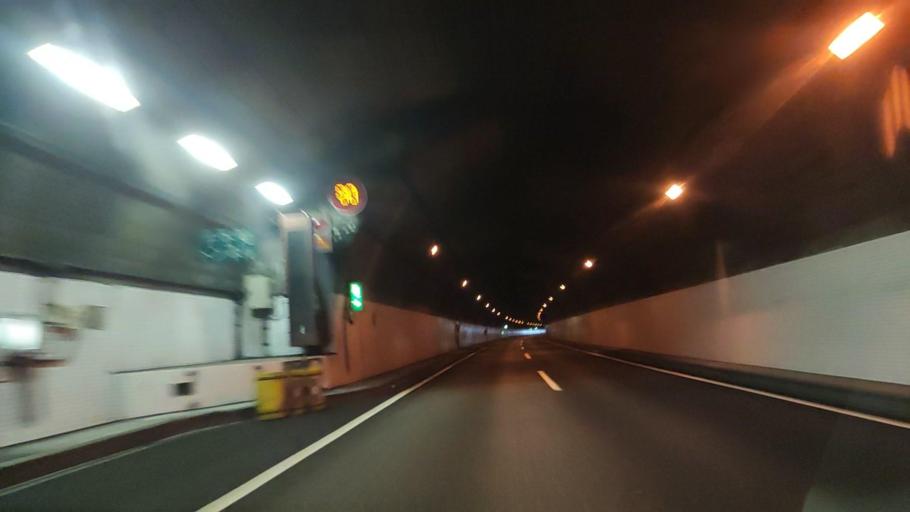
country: JP
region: Niigata
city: Itoigawa
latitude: 37.0180
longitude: 137.7827
